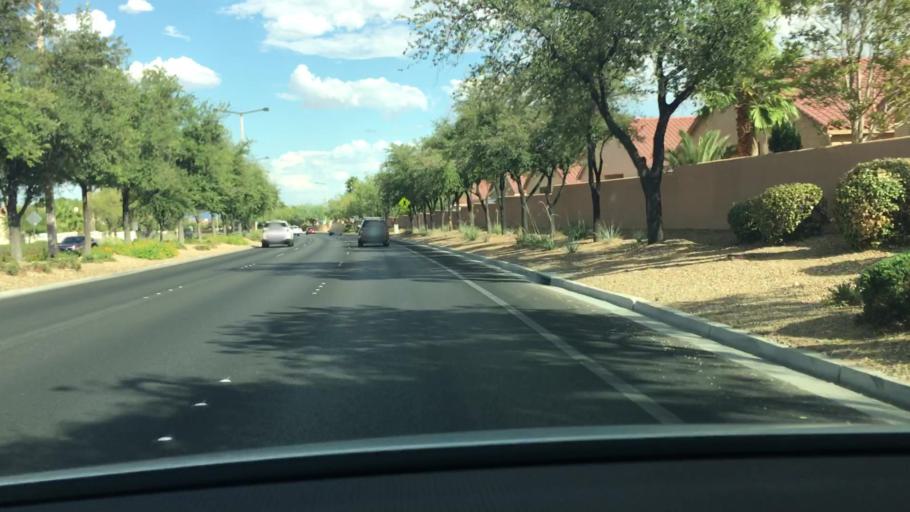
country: US
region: Nevada
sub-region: Clark County
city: Spring Valley
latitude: 36.1972
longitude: -115.2773
